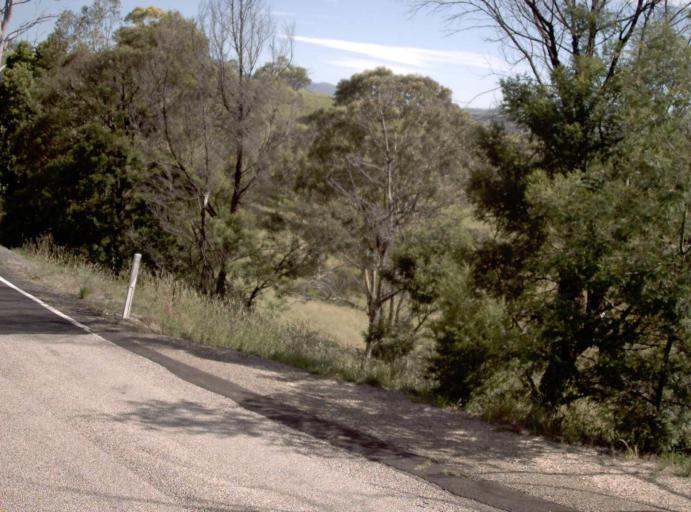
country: AU
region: Victoria
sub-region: East Gippsland
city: Lakes Entrance
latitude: -37.5138
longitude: 148.1677
